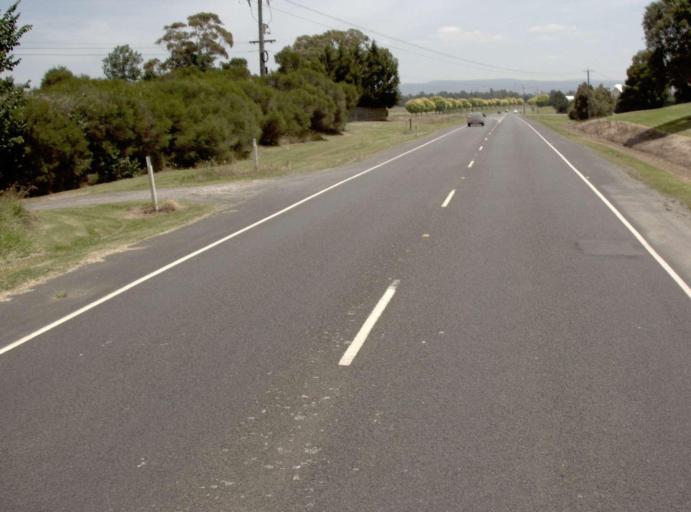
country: AU
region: Victoria
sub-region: Latrobe
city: Traralgon
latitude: -38.2116
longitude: 146.5456
